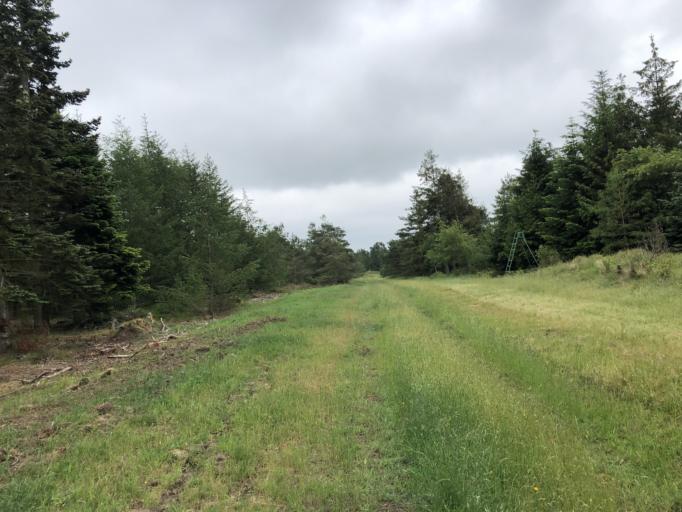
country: DK
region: Central Jutland
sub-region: Holstebro Kommune
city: Ulfborg
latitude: 56.2499
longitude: 8.3618
